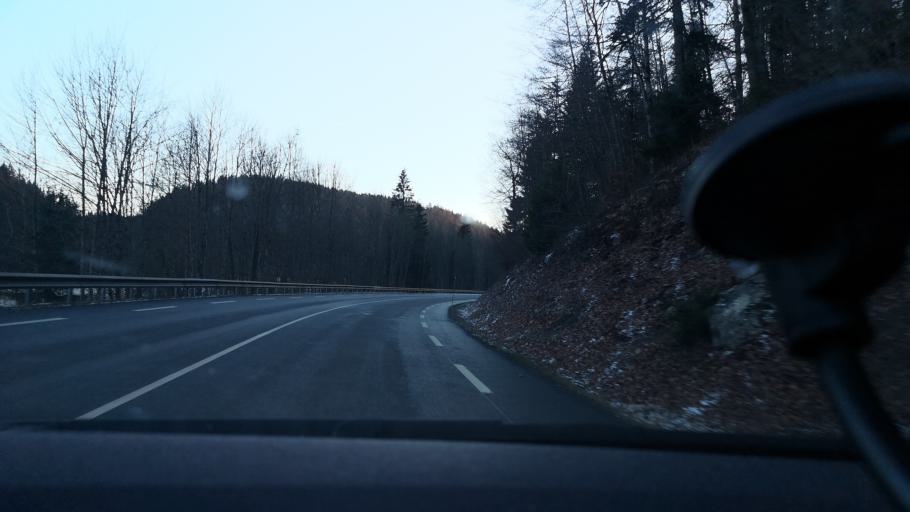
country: FR
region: Franche-Comte
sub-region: Departement du Doubs
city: La Cluse-et-Mijoux
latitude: 46.8703
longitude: 6.3642
